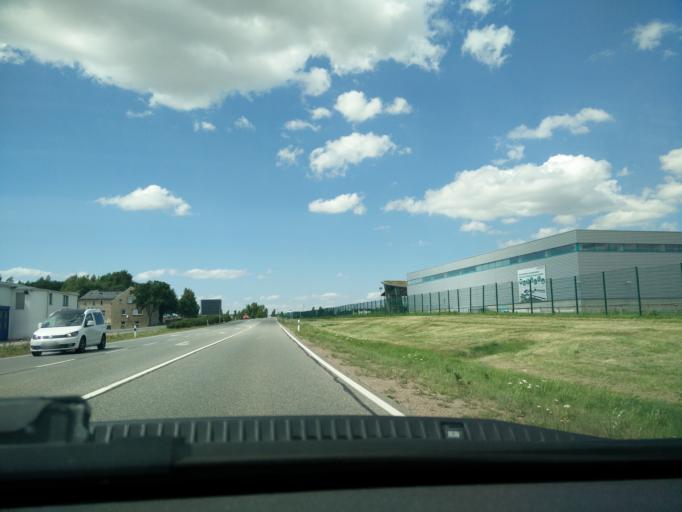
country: DE
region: Saxony
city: Hartmannsdorf
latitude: 50.8925
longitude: 12.7886
